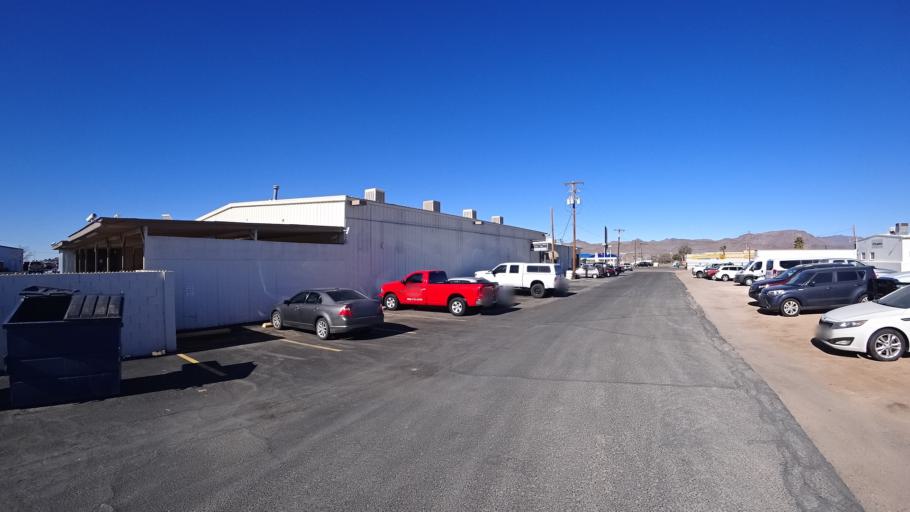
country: US
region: Arizona
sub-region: Mohave County
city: Kingman
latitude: 35.2084
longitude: -114.0170
